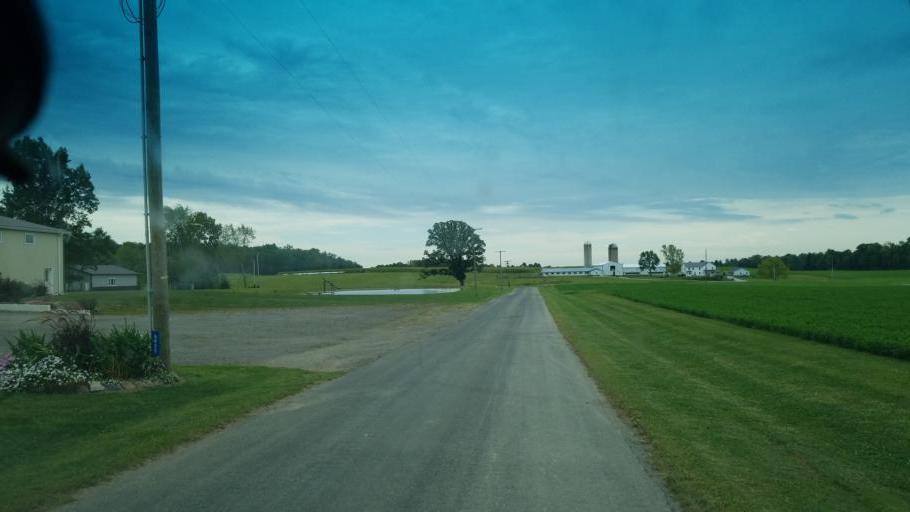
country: US
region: Ohio
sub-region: Huron County
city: Greenwich
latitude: 40.9334
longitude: -82.5095
